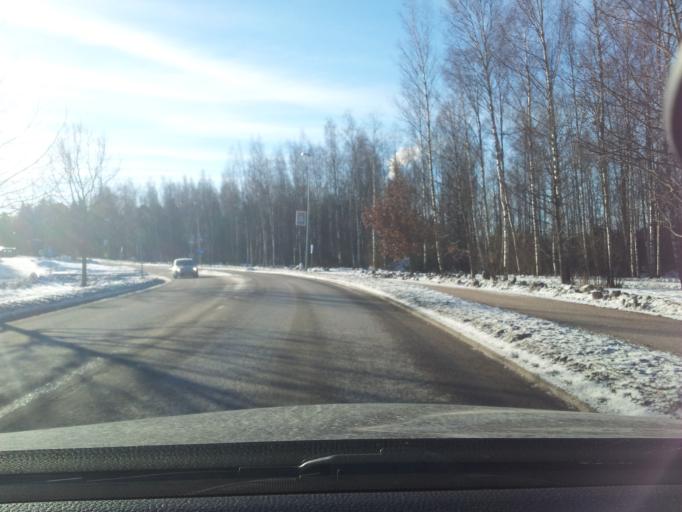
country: FI
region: Uusimaa
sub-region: Helsinki
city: Koukkuniemi
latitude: 60.1589
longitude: 24.7256
